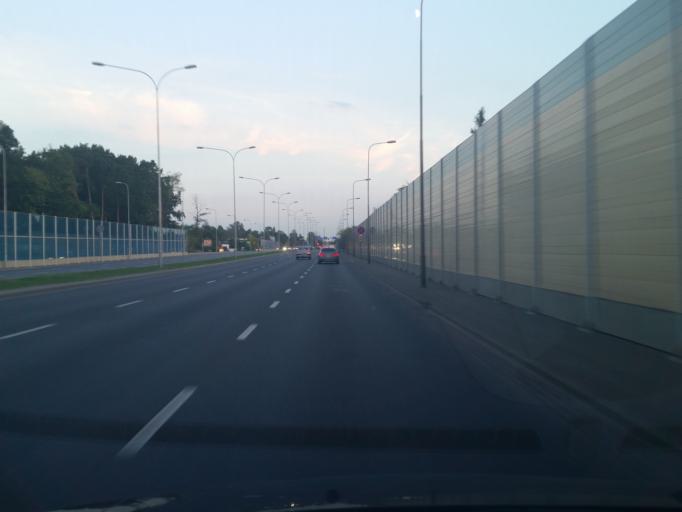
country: PL
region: Masovian Voivodeship
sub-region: Powiat legionowski
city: Jablonna
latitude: 52.3540
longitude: 20.9426
